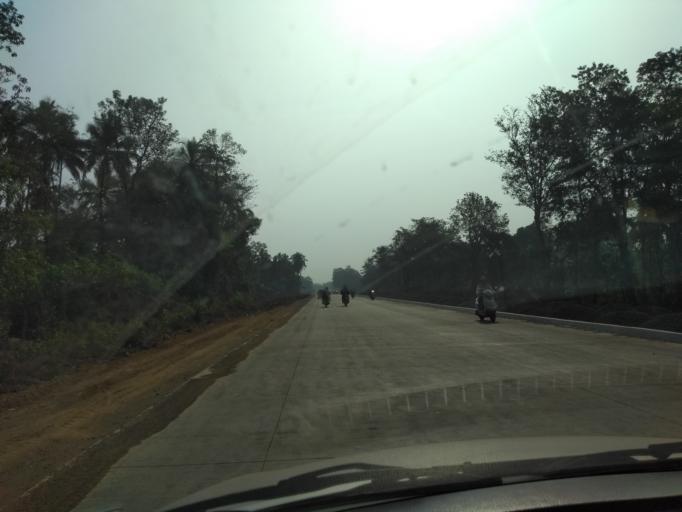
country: IN
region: Maharashtra
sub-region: Sindhudurg
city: Kudal
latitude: 15.9695
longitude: 73.7224
